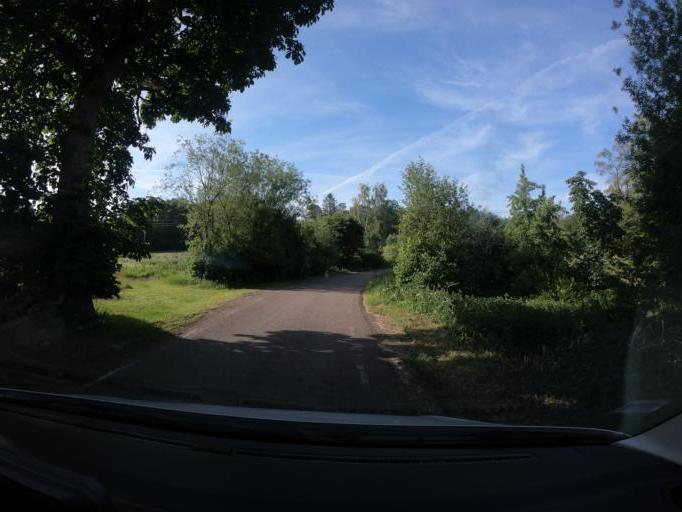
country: SE
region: Skane
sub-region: Orkelljunga Kommun
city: OErkelljunga
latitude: 56.3444
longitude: 13.1226
